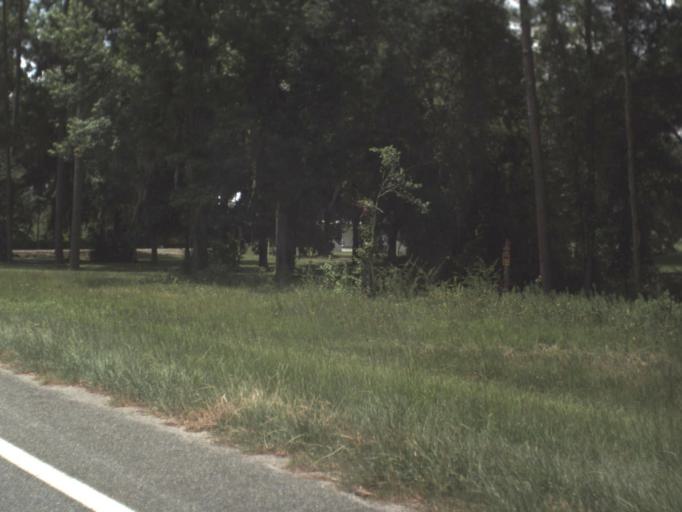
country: US
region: Florida
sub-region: Hamilton County
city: Jasper
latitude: 30.5263
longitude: -83.0306
